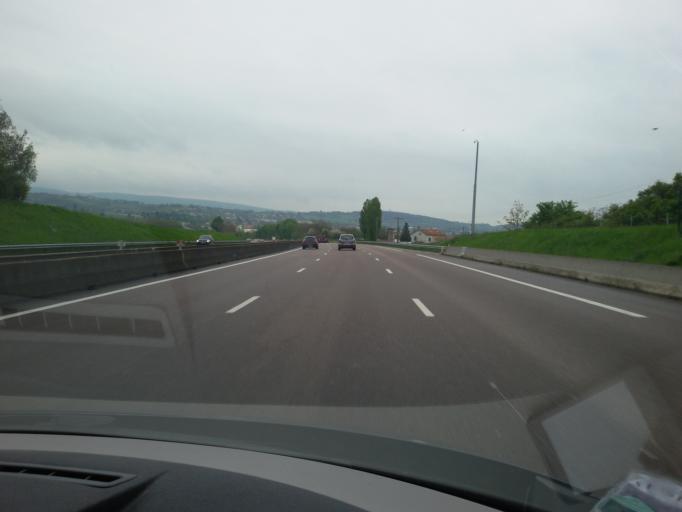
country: FR
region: Bourgogne
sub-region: Departement de Saone-et-Loire
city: Tournus
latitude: 46.5439
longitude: 4.9173
